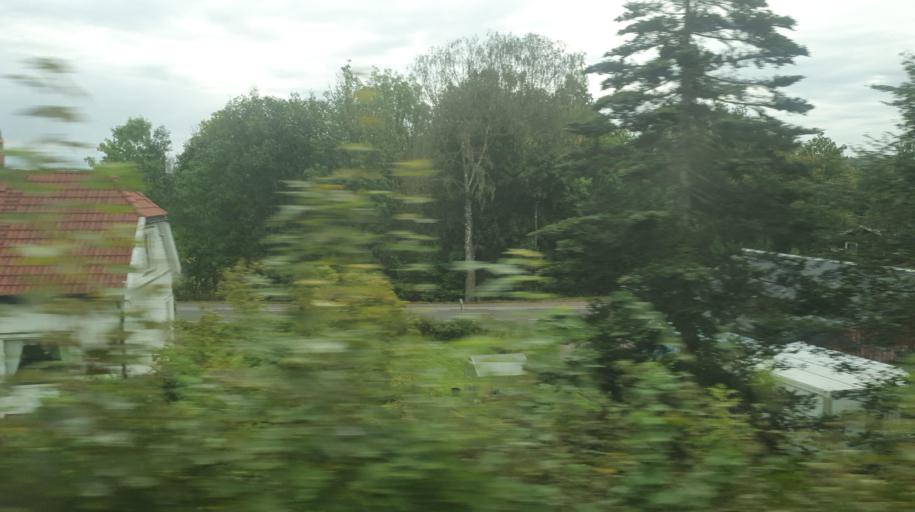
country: NO
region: Vestfold
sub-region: Horten
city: Skoppum
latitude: 59.3874
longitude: 10.4097
